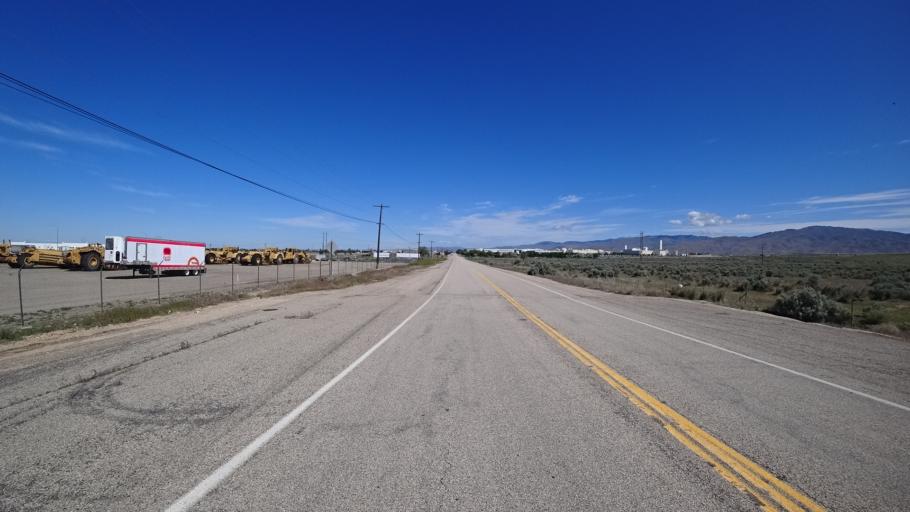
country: US
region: Idaho
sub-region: Ada County
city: Boise
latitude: 43.5135
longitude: -116.1434
